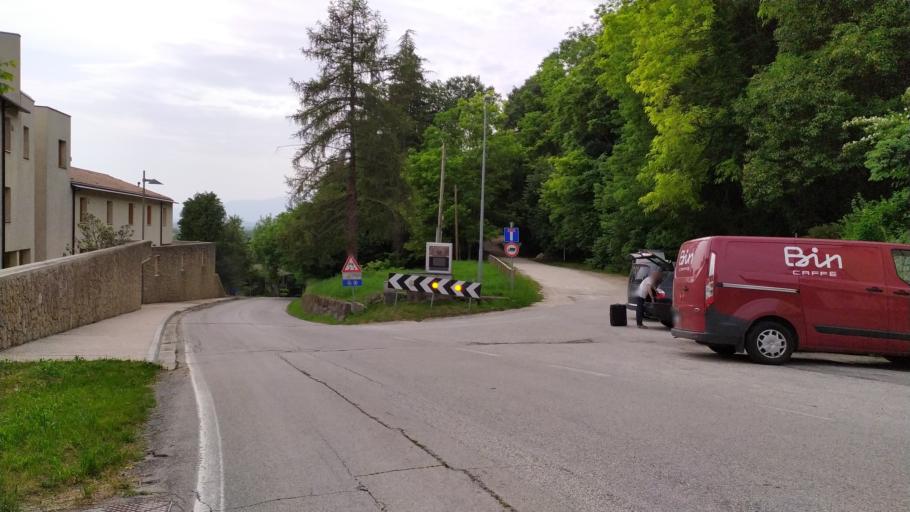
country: IT
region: Veneto
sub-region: Provincia di Treviso
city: Barbisano
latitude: 45.8731
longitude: 12.1950
